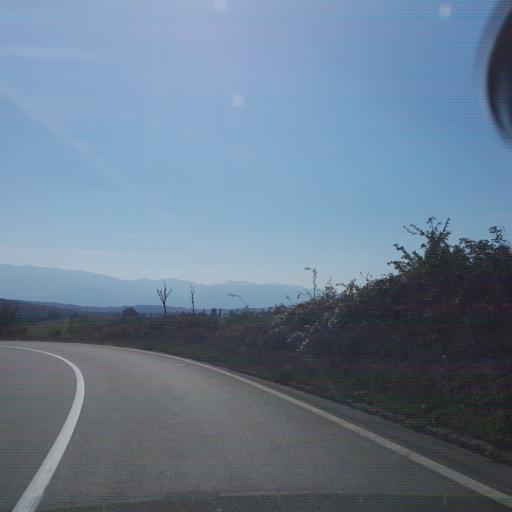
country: RS
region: Central Serbia
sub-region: Zajecarski Okrug
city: Knjazevac
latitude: 43.4777
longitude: 22.2291
